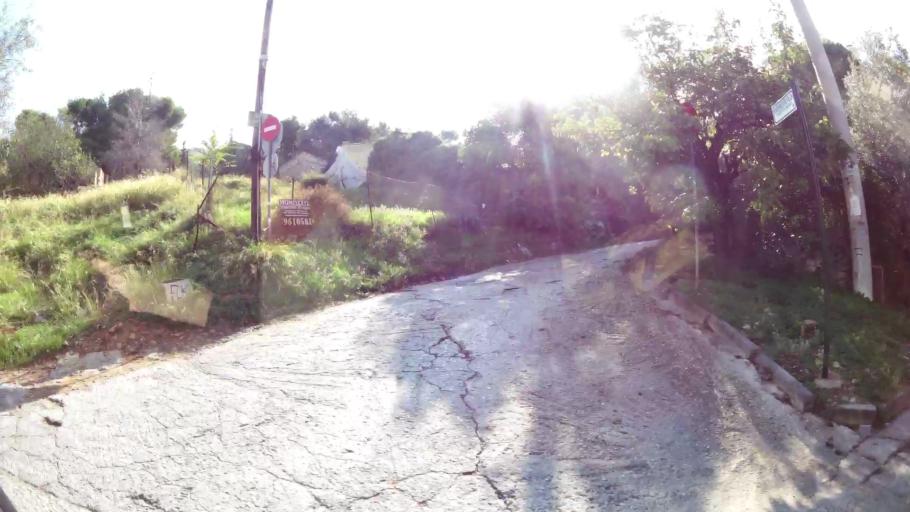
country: GR
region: Attica
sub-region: Nomarchia Athinas
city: Ilioupoli
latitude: 37.9325
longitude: 23.7632
